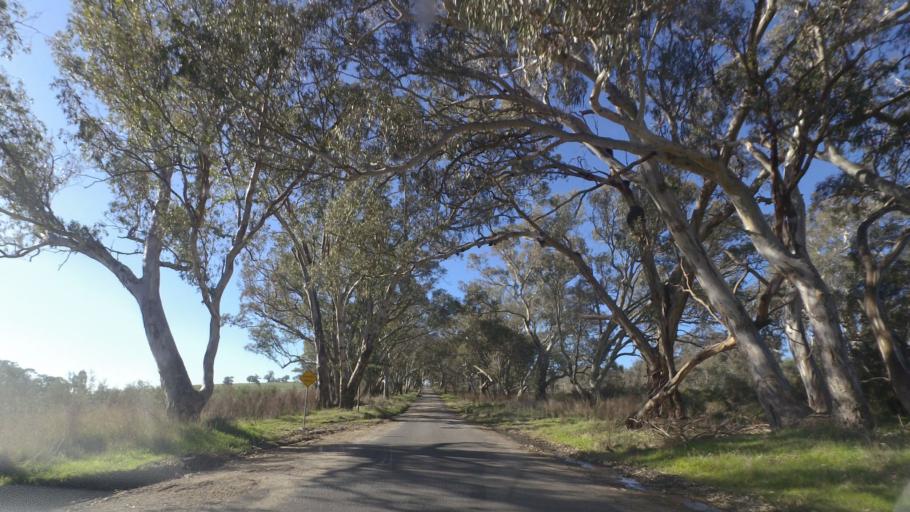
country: AU
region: Victoria
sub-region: Mount Alexander
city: Castlemaine
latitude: -36.9636
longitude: 144.3279
